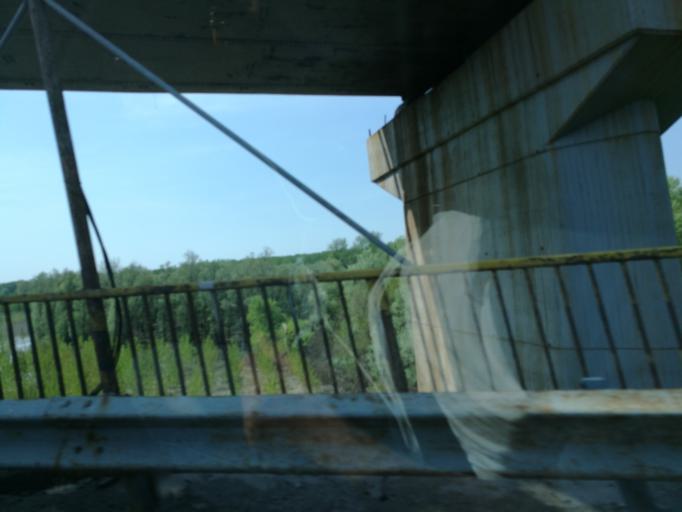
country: RO
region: Constanta
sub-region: Oras Cernavoda
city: Cernavoda
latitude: 44.3430
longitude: 28.0055
